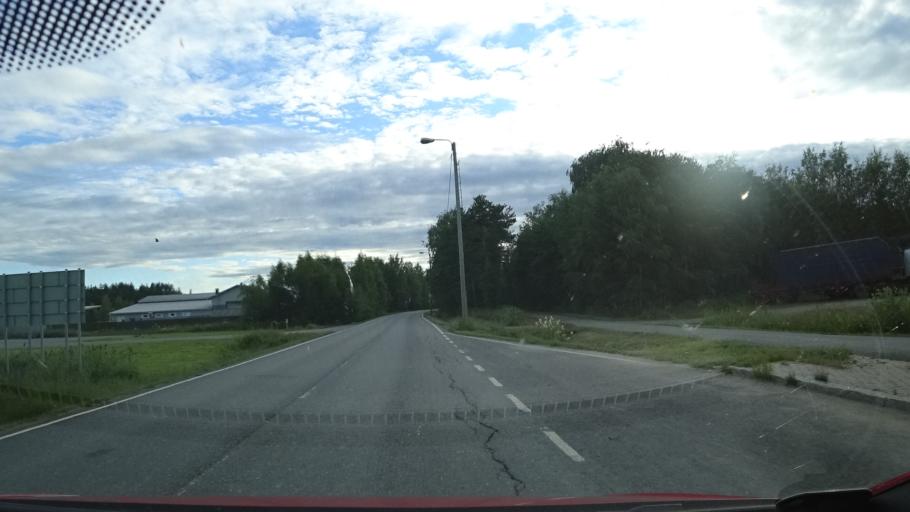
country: FI
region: Northern Ostrobothnia
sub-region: Oulu
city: Liminka
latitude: 64.8086
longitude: 25.4533
